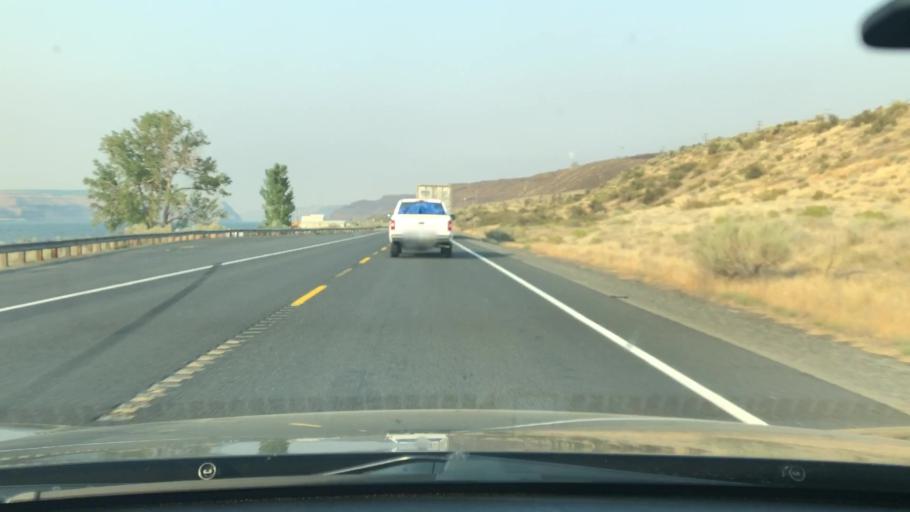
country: US
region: Oregon
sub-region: Umatilla County
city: Stanfield
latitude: 45.9286
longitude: -119.1011
